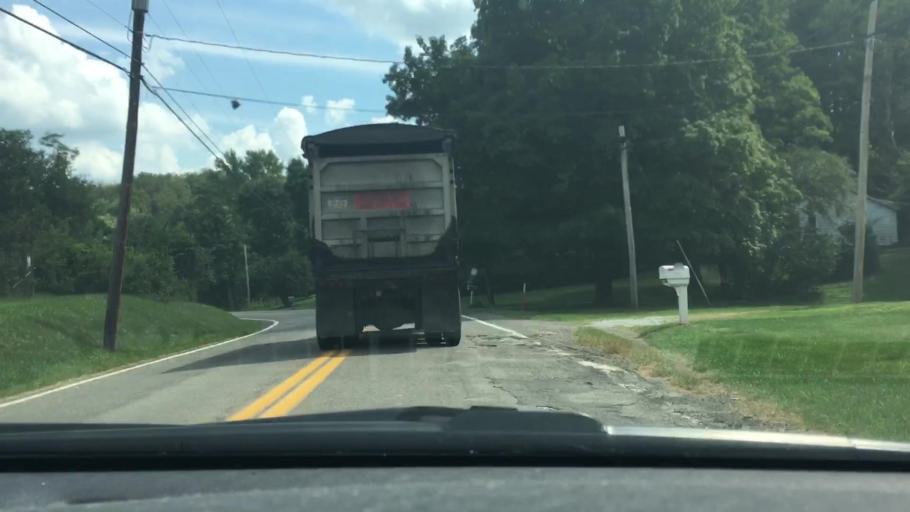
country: US
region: Pennsylvania
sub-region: Washington County
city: Gastonville
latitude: 40.2531
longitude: -79.9690
